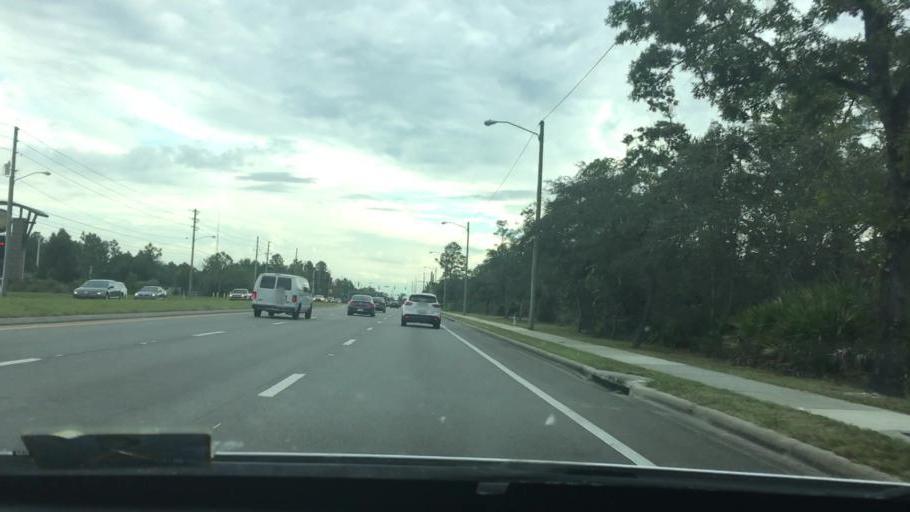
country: US
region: Florida
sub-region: Orange County
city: Alafaya
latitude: 28.6048
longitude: -81.2078
